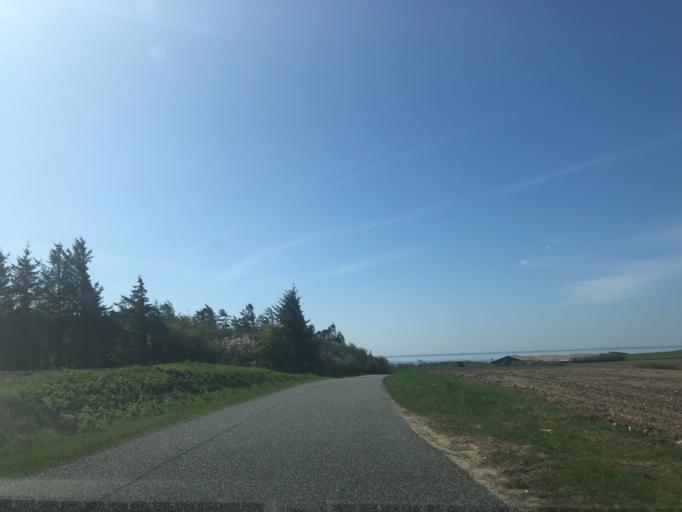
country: DK
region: Central Jutland
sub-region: Holstebro Kommune
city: Vinderup
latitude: 56.5695
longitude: 8.7680
